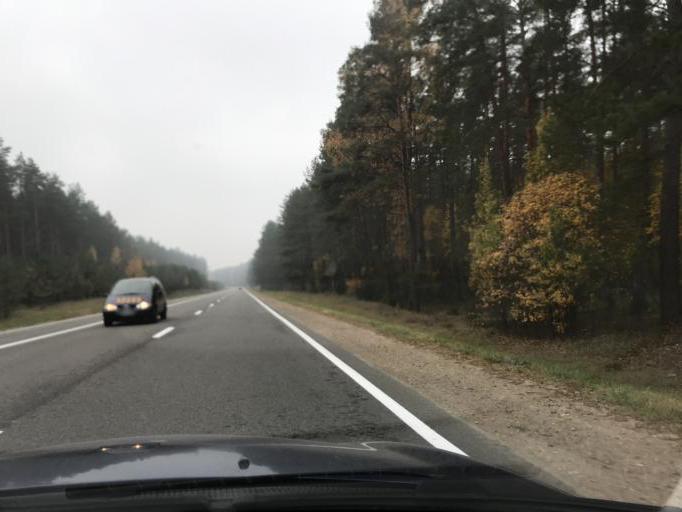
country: LT
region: Alytaus apskritis
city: Druskininkai
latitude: 53.9230
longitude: 23.9303
